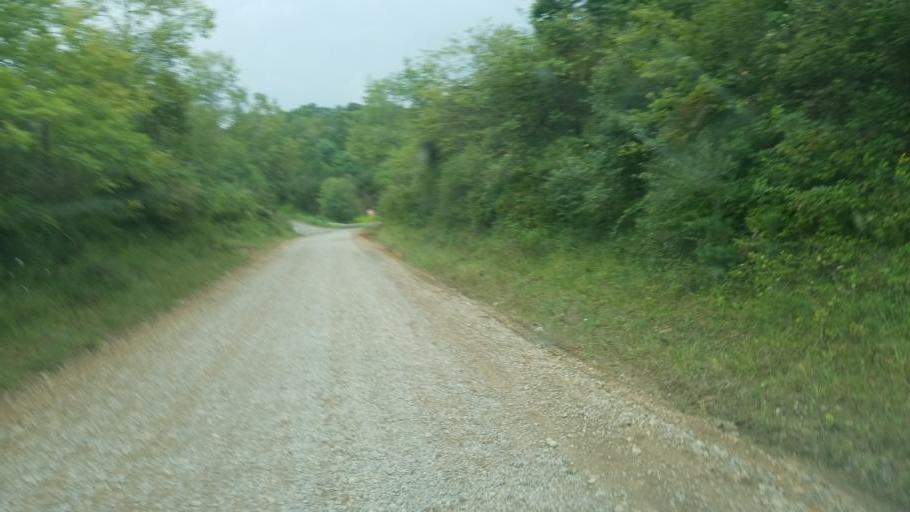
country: US
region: Pennsylvania
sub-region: Clarion County
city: Marianne
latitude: 41.1552
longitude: -79.4663
